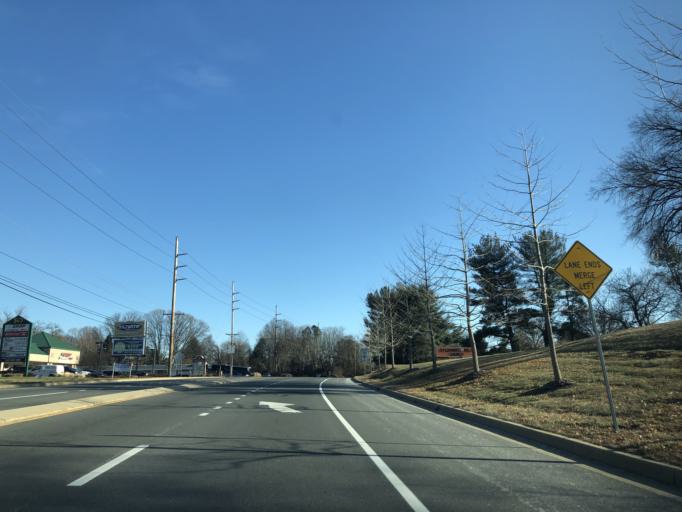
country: US
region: Delaware
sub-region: New Castle County
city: Hockessin
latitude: 39.7861
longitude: -75.6870
